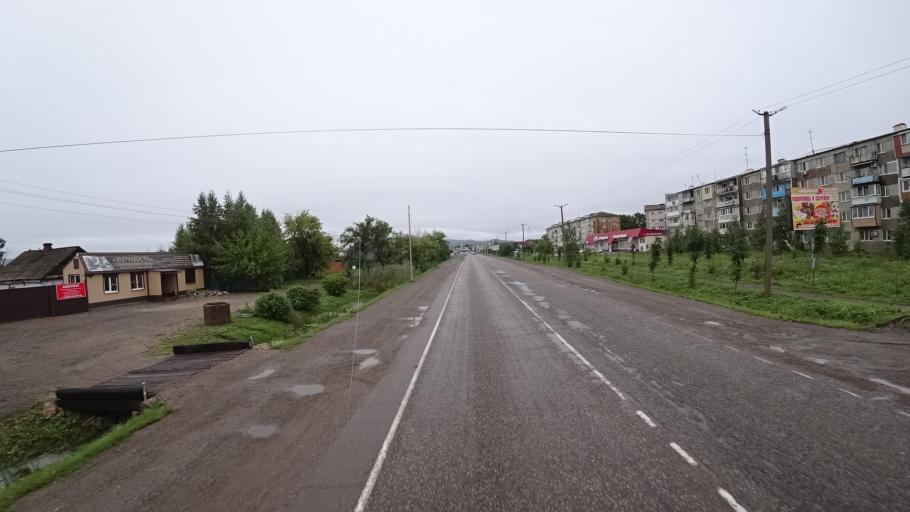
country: RU
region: Primorskiy
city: Monastyrishche
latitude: 44.2064
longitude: 132.4501
